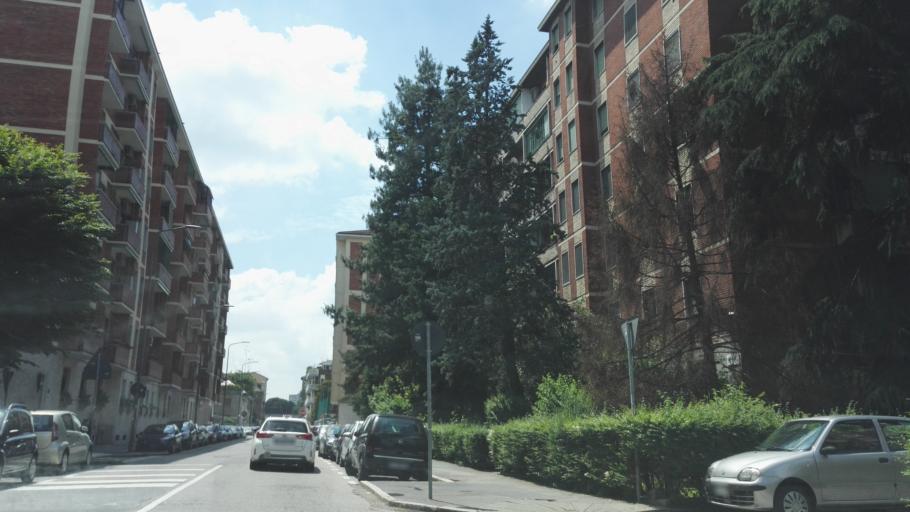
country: IT
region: Lombardy
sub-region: Citta metropolitana di Milano
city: Chiaravalle
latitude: 45.4426
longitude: 9.2275
